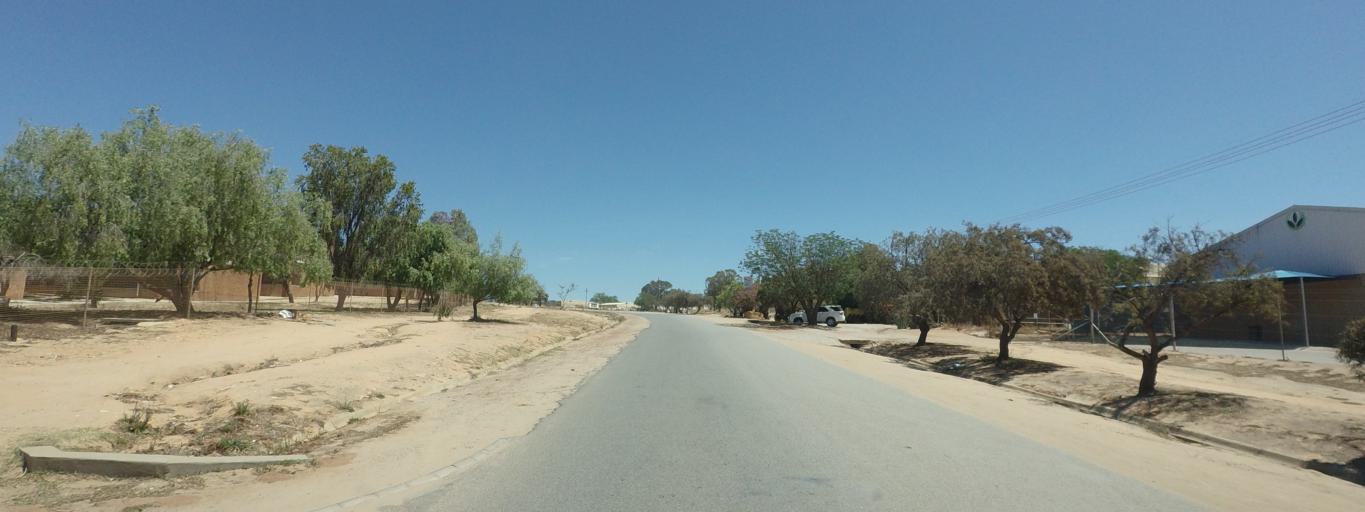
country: ZA
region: Western Cape
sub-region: West Coast District Municipality
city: Clanwilliam
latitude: -32.1886
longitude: 18.8893
